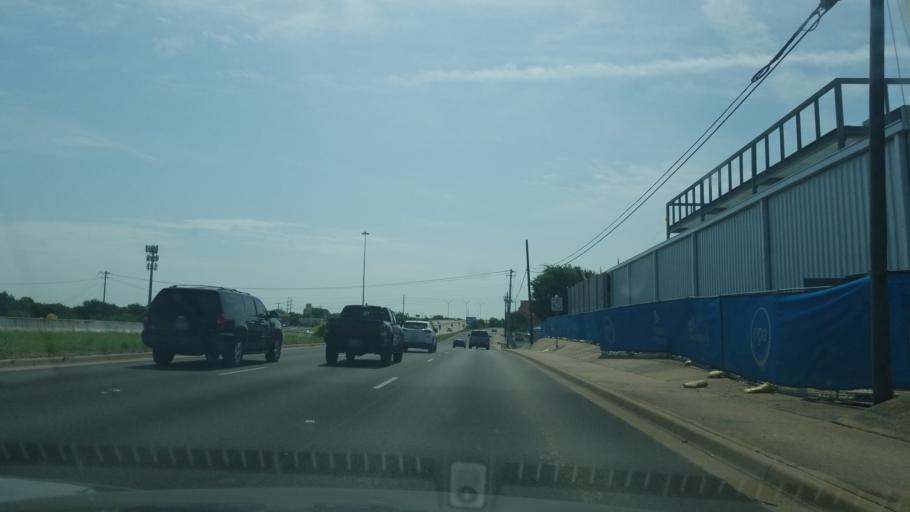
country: US
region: Texas
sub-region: Travis County
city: Austin
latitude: 30.2157
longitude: -97.7428
